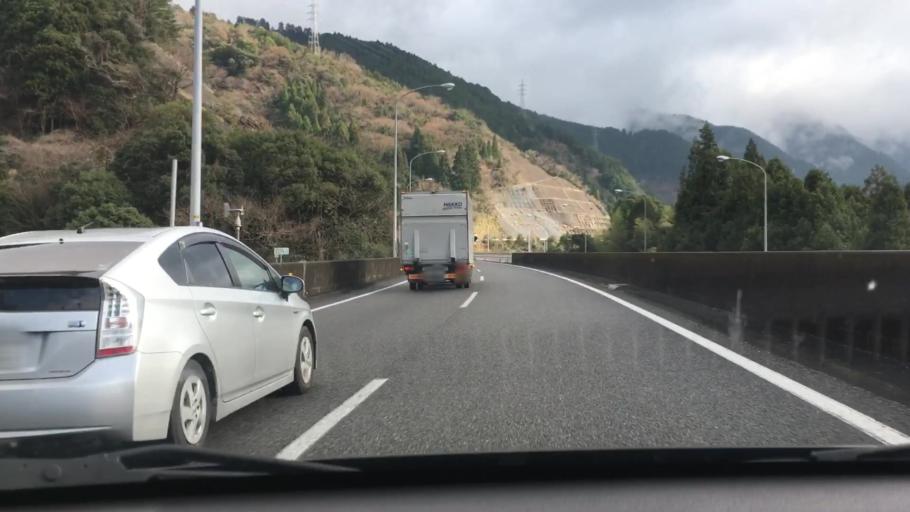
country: JP
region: Kumamoto
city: Yatsushiro
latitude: 32.4012
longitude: 130.6994
